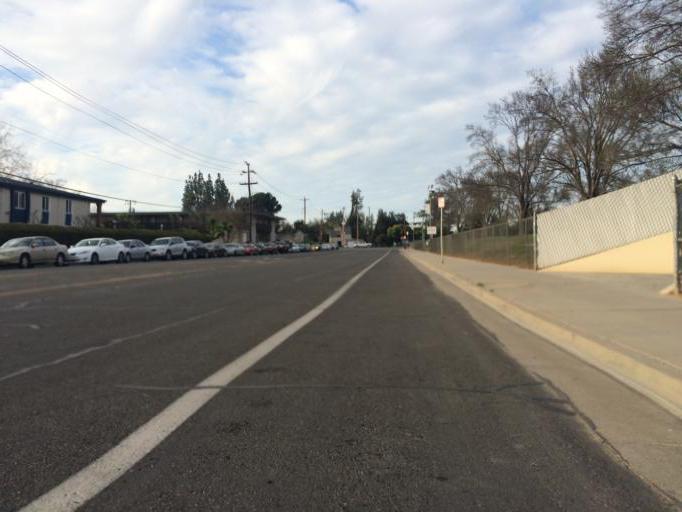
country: US
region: California
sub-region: Fresno County
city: Clovis
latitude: 36.8142
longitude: -119.7609
